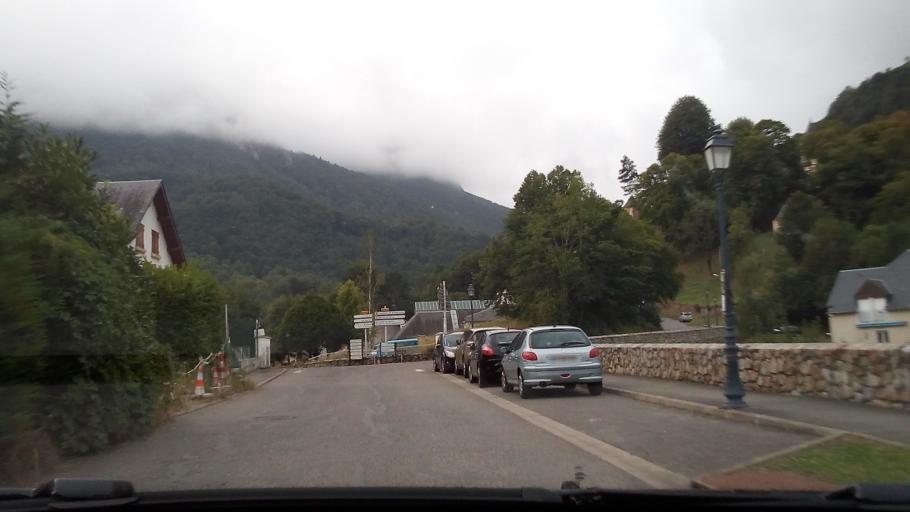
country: FR
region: Midi-Pyrenees
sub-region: Departement des Hautes-Pyrenees
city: Cauterets
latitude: 42.9519
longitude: -0.2153
